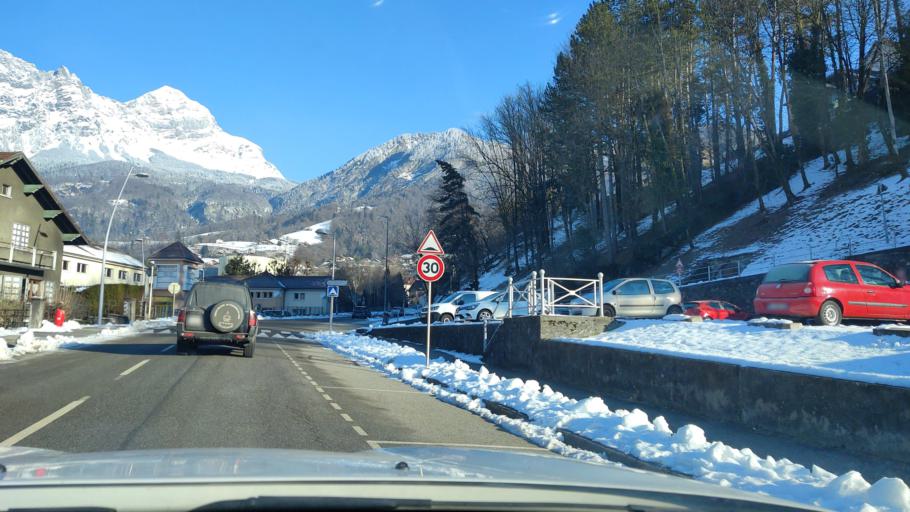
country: FR
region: Rhone-Alpes
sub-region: Departement de la Savoie
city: Ugine
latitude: 45.7515
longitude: 6.4174
